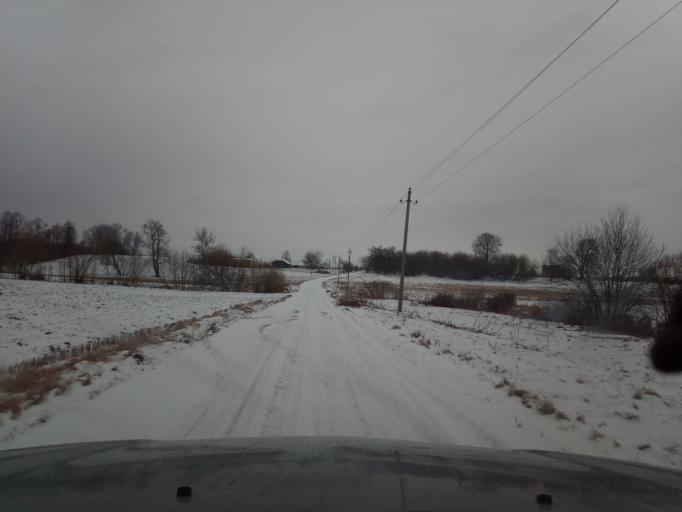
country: LT
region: Vilnius County
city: Ukmerge
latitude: 55.4786
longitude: 24.6248
